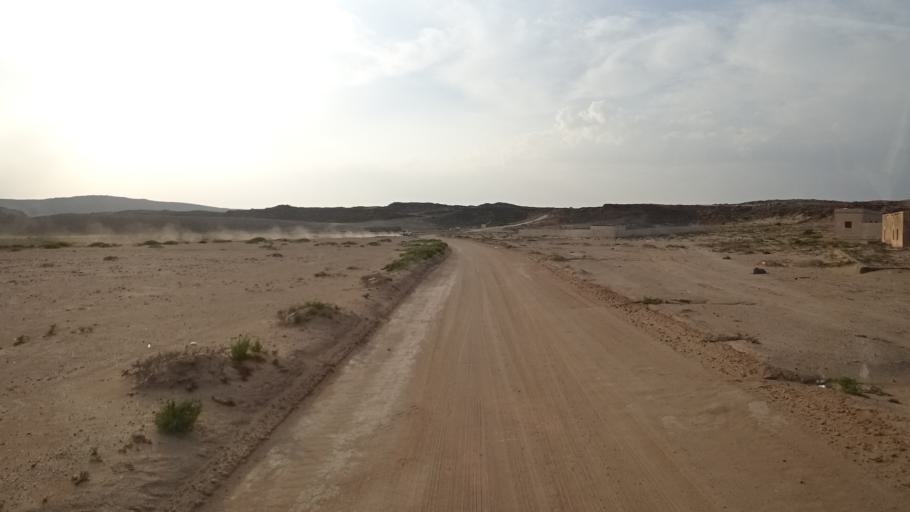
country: OM
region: Ash Sharqiyah
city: Sur
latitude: 22.4495
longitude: 59.8269
